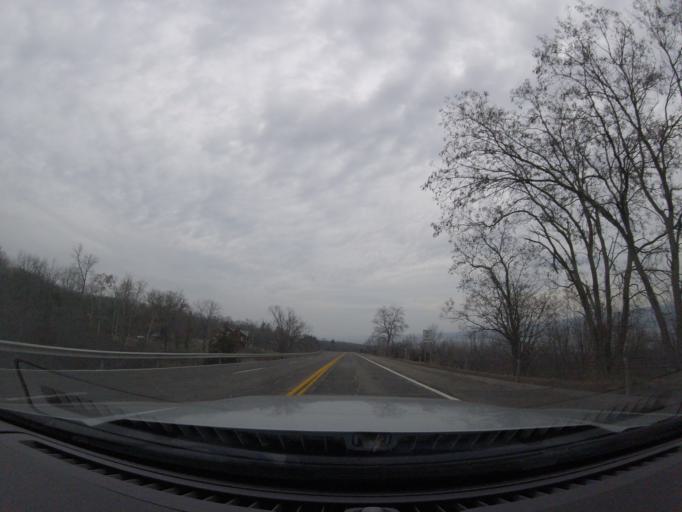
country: US
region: New York
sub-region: Yates County
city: Dundee
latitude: 42.5276
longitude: -76.9180
